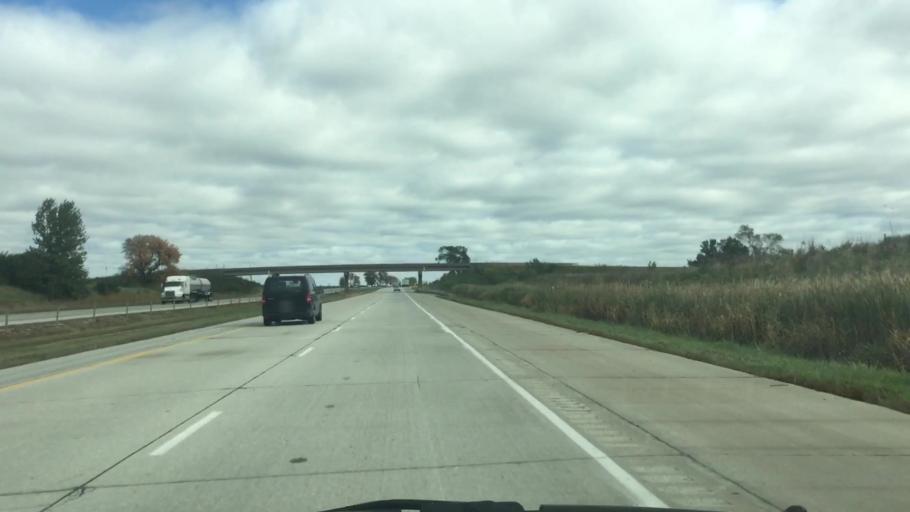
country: US
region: Iowa
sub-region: Polk County
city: Mitchellville
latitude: 41.6789
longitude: -93.4089
